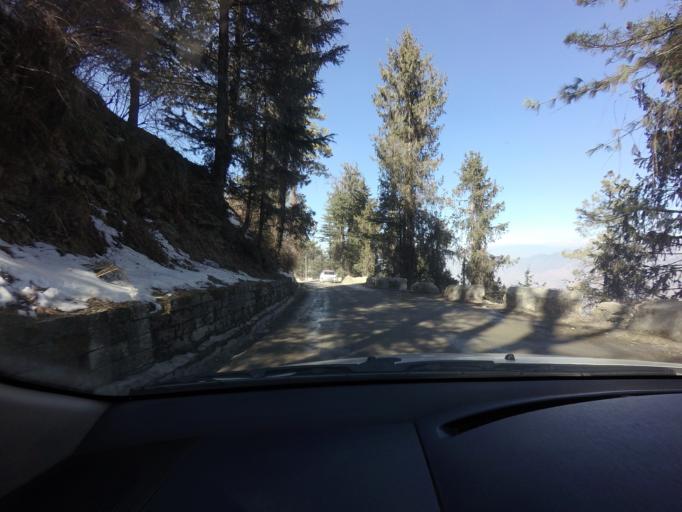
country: IN
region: Himachal Pradesh
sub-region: Shimla
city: Theog
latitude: 31.1005
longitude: 77.2660
